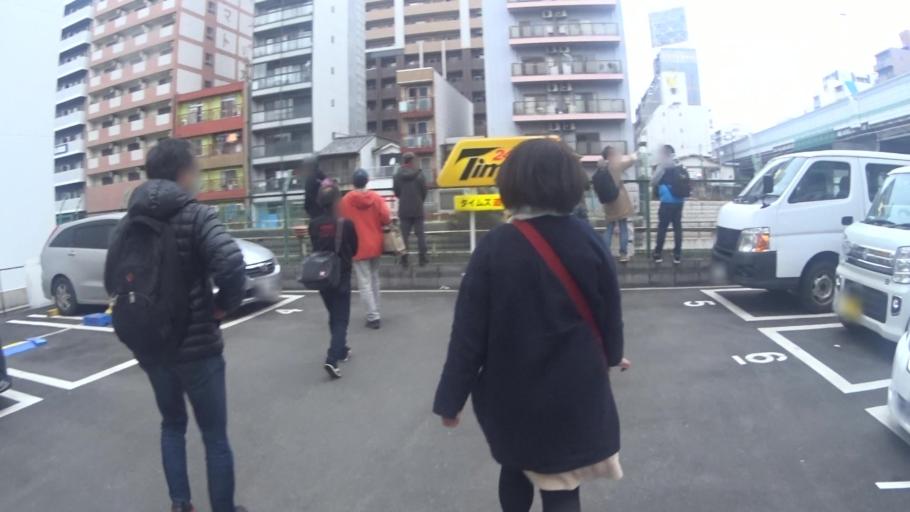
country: JP
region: Osaka
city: Osaka-shi
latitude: 34.6684
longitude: 135.5102
